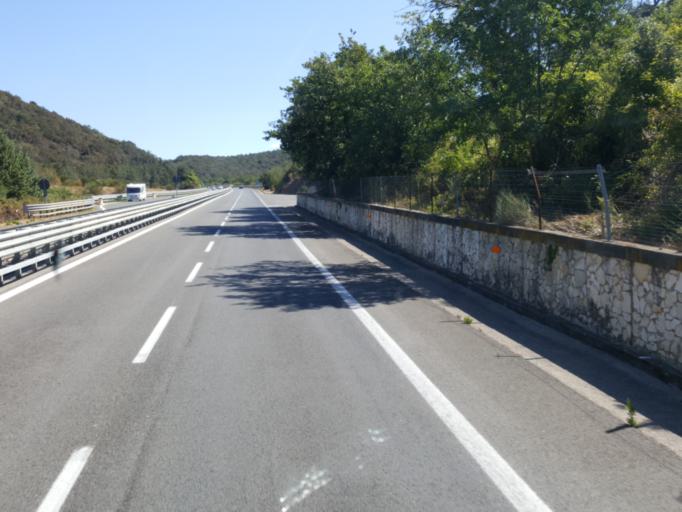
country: IT
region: Tuscany
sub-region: Provincia di Grosseto
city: Bagno Roselle
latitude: 42.8562
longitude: 11.1794
